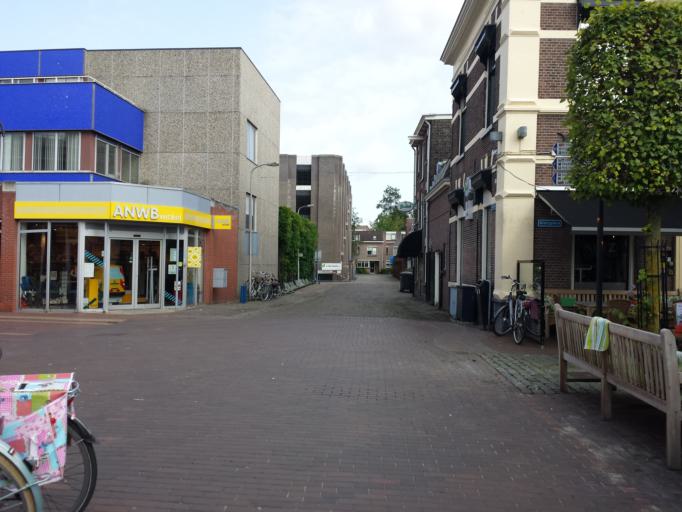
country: NL
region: Overijssel
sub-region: Gemeente Almelo
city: Almelo
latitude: 52.3565
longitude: 6.6634
